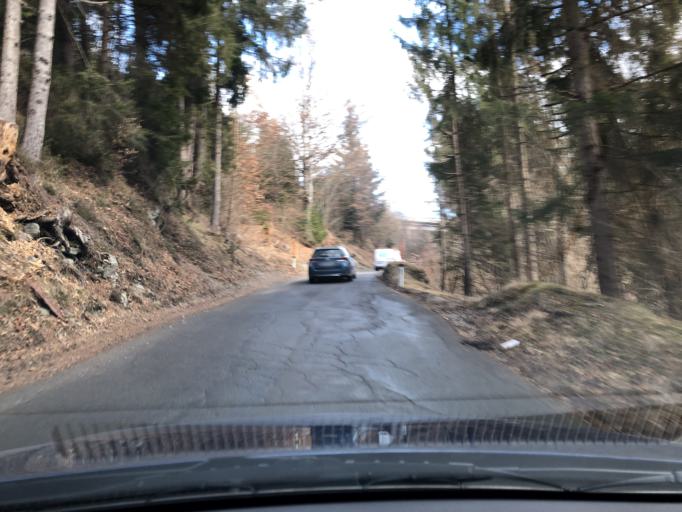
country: AT
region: Carinthia
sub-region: Politischer Bezirk Villach Land
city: Paternion
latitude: 46.7032
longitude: 13.6349
